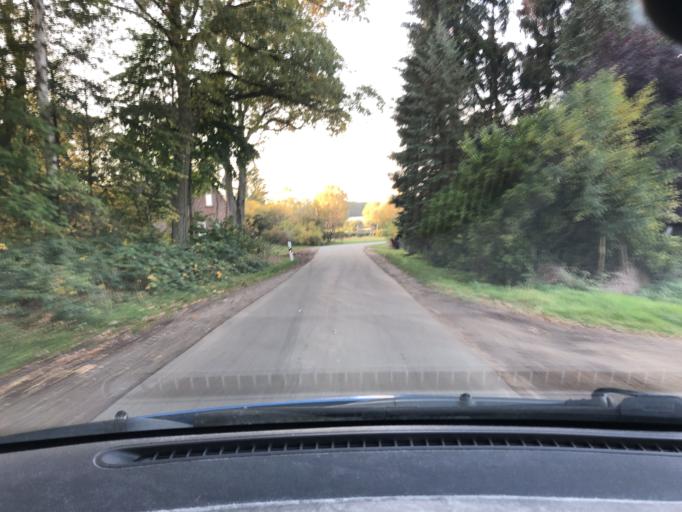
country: DE
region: Lower Saxony
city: Hitzacker
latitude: 53.1450
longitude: 11.0047
